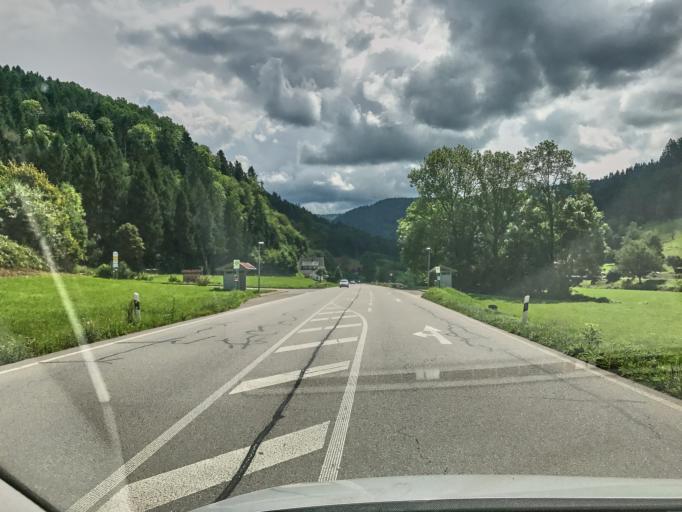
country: DE
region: Baden-Wuerttemberg
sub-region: Freiburg Region
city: Wolfach
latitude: 48.2980
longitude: 8.2565
